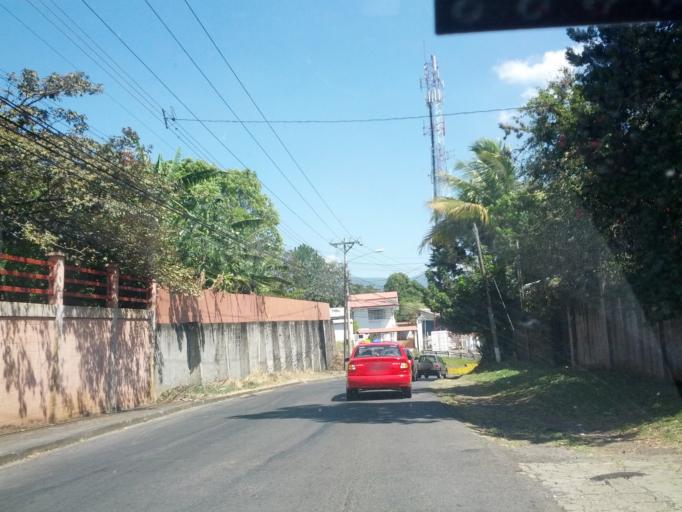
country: CR
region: Alajuela
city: Alajuela
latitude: 10.0232
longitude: -84.2190
